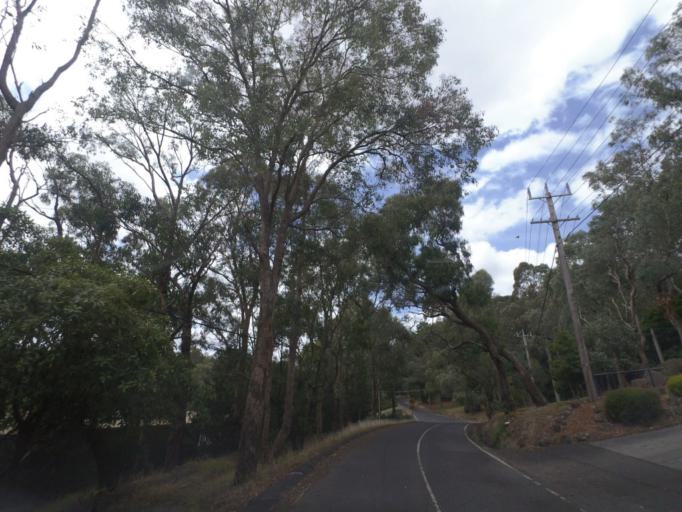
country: AU
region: Victoria
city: Mitcham
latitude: -37.7991
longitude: 145.2069
